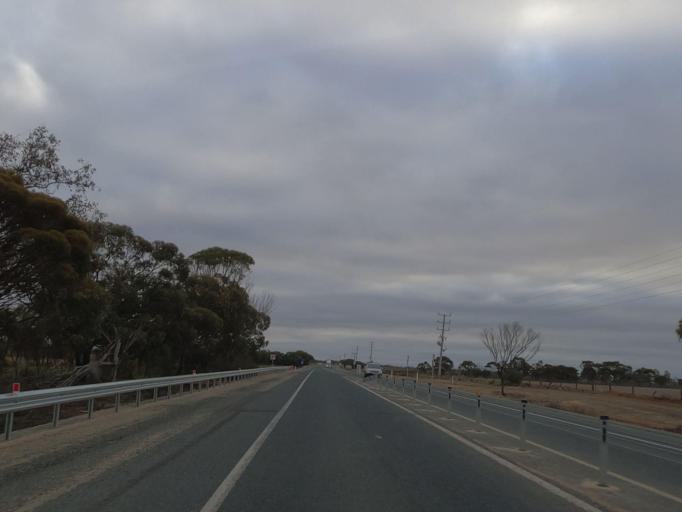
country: AU
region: Victoria
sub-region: Swan Hill
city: Swan Hill
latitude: -35.5472
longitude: 143.7625
